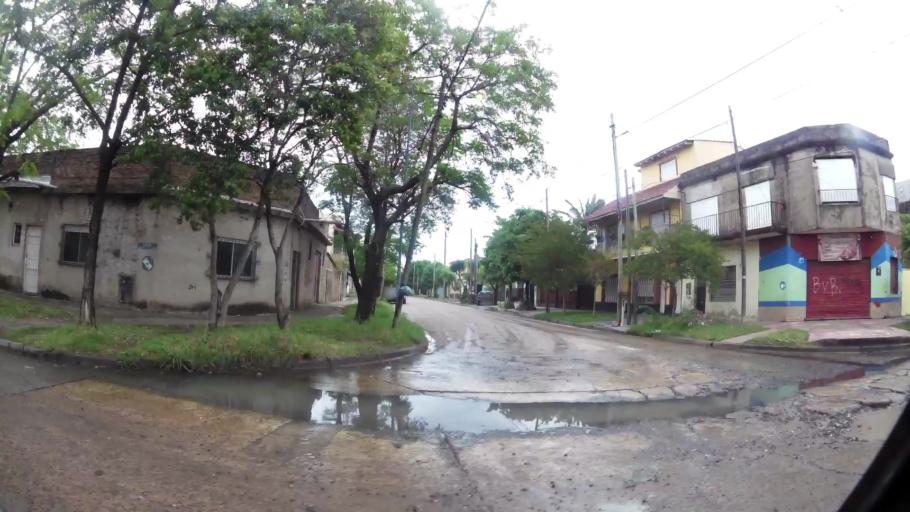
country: AR
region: Buenos Aires
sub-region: Partido de Lanus
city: Lanus
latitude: -34.7304
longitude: -58.3651
